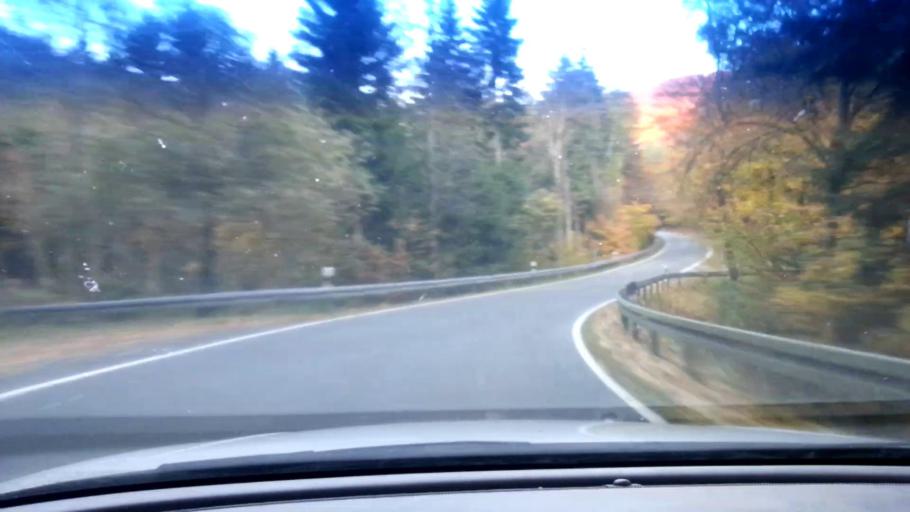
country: DE
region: Bavaria
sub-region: Upper Franconia
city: Heiligenstadt
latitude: 49.8625
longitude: 11.1266
